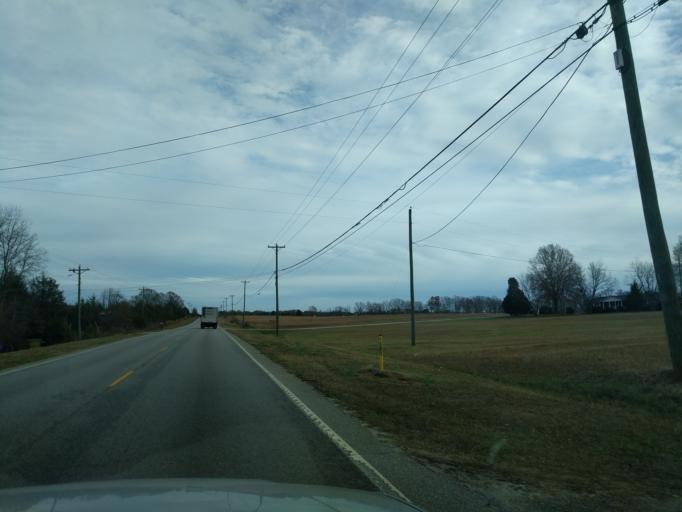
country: US
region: South Carolina
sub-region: Anderson County
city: Williamston
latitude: 34.6346
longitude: -82.4140
